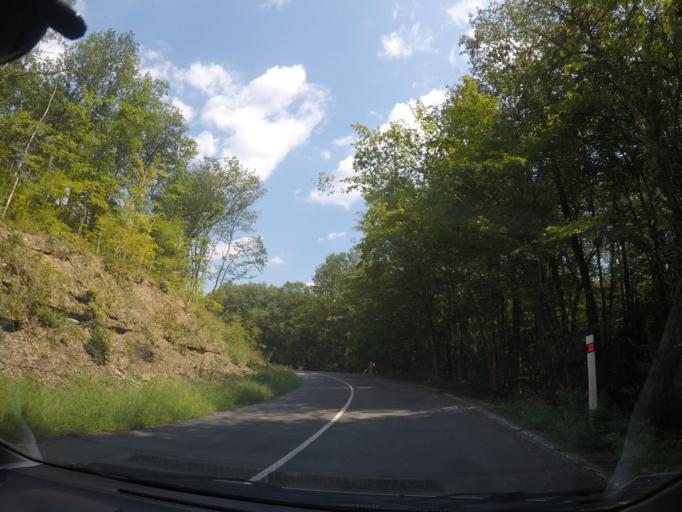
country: SK
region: Banskobystricky
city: Dudince
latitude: 48.2586
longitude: 18.8607
